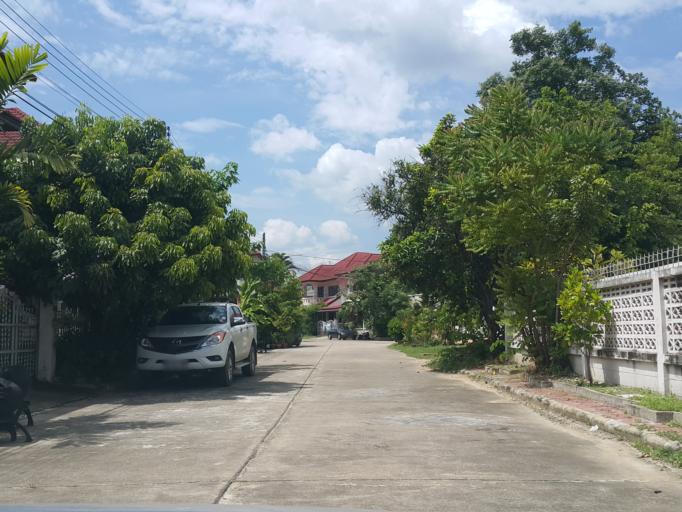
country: TH
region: Chiang Mai
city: Hang Dong
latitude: 18.7389
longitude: 98.9422
